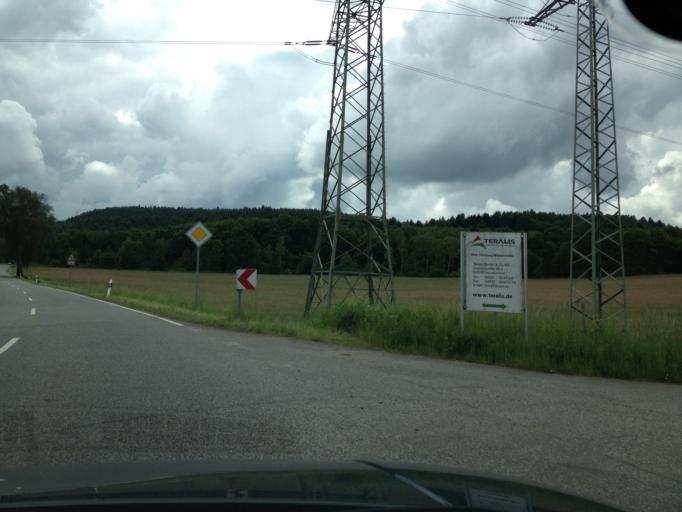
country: DE
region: Saarland
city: Homburg
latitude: 49.3006
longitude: 7.2974
